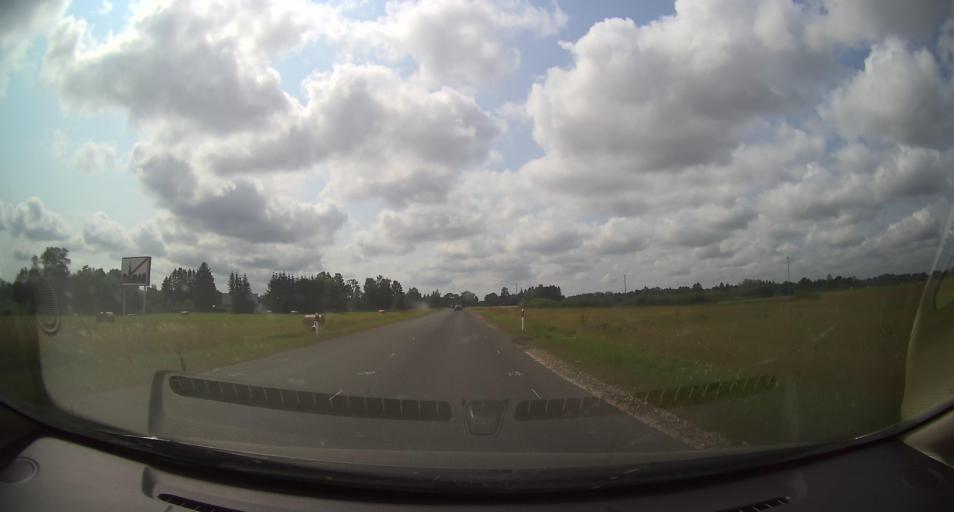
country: EE
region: Paernumaa
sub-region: Audru vald
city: Audru
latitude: 58.4695
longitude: 24.3204
